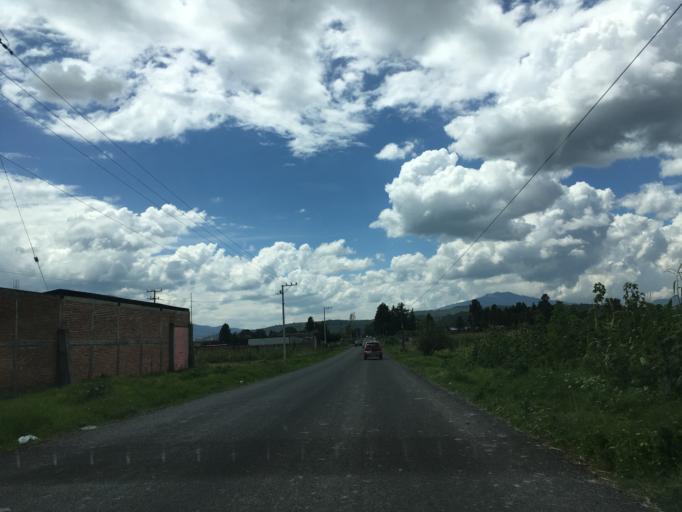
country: MX
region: Michoacan
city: Zacapu
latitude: 19.8401
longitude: -101.7523
